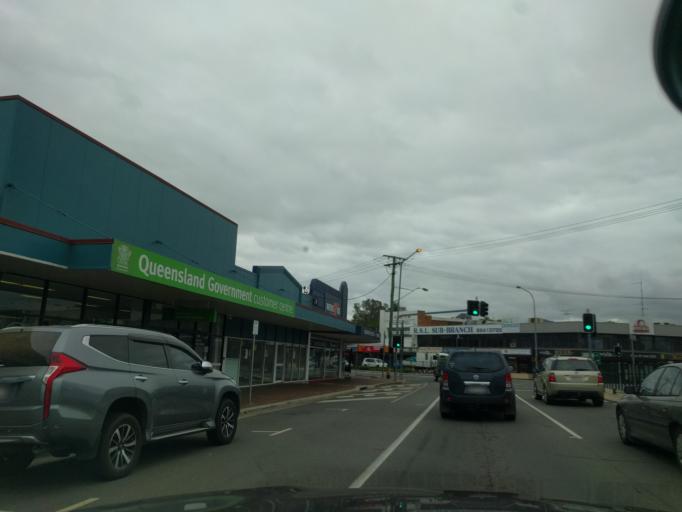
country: AU
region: Queensland
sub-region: Logan
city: Cedar Vale
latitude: -27.9885
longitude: 152.9955
